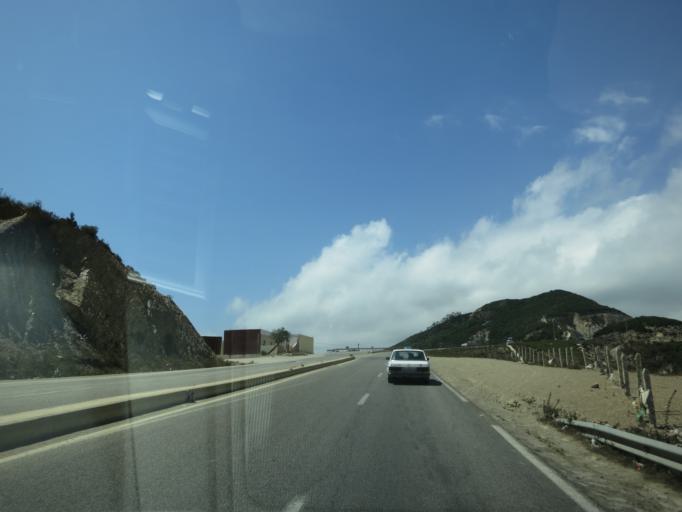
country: ES
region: Ceuta
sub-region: Ceuta
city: Ceuta
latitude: 35.8677
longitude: -5.3762
